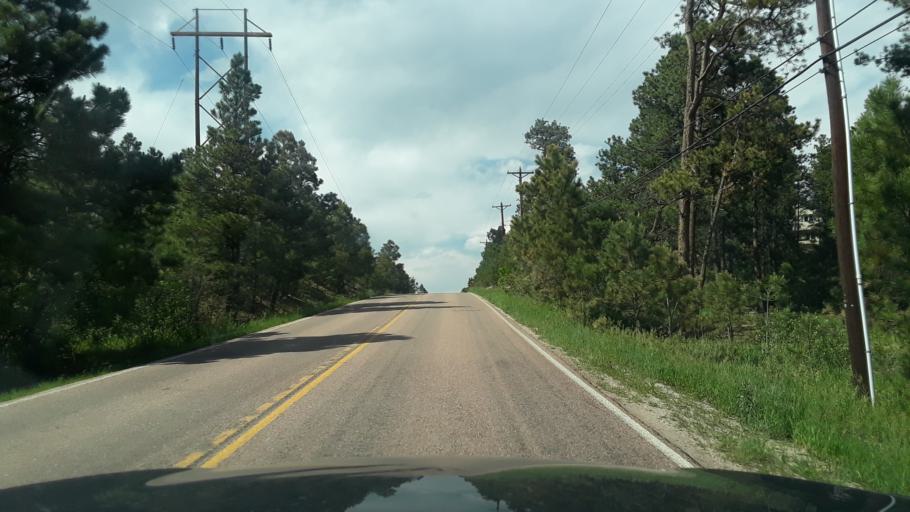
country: US
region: Colorado
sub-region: El Paso County
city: Gleneagle
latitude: 39.0431
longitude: -104.7849
